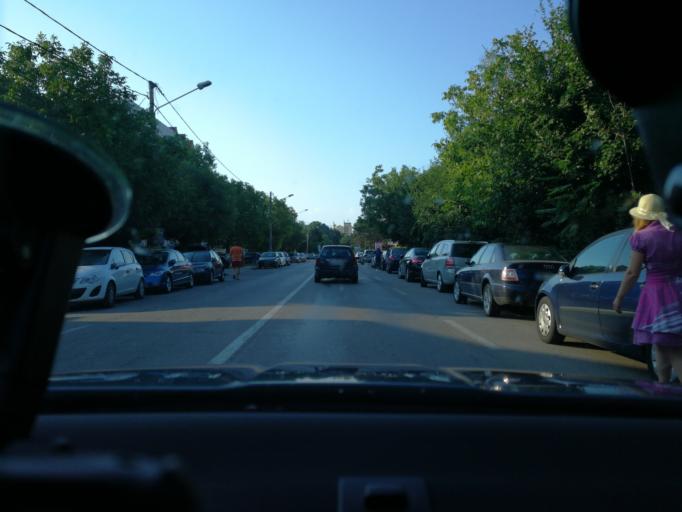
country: RO
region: Constanta
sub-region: Oras Eforie
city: Eforie Nord
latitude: 44.0704
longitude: 28.6306
